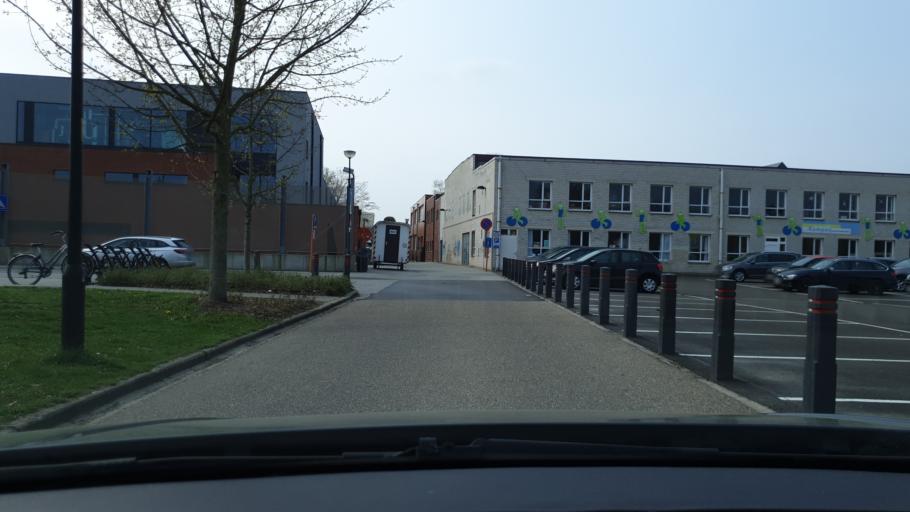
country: BE
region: Flanders
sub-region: Provincie Antwerpen
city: Geel
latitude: 51.1581
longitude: 4.9906
